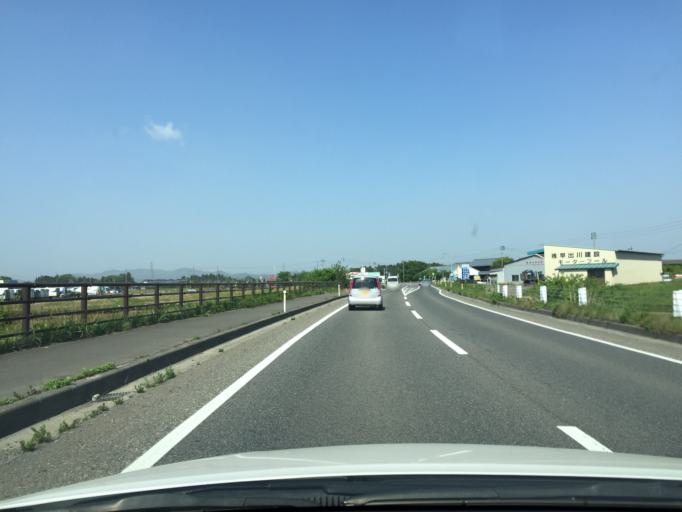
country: JP
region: Niigata
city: Gosen
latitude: 37.7482
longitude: 139.2137
